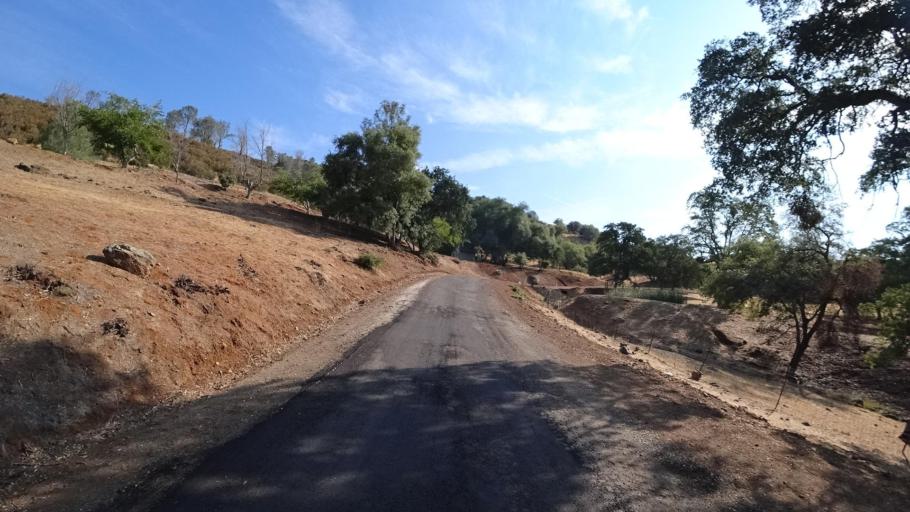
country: US
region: California
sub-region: Tuolumne County
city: Tuolumne City
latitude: 37.7246
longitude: -120.2622
